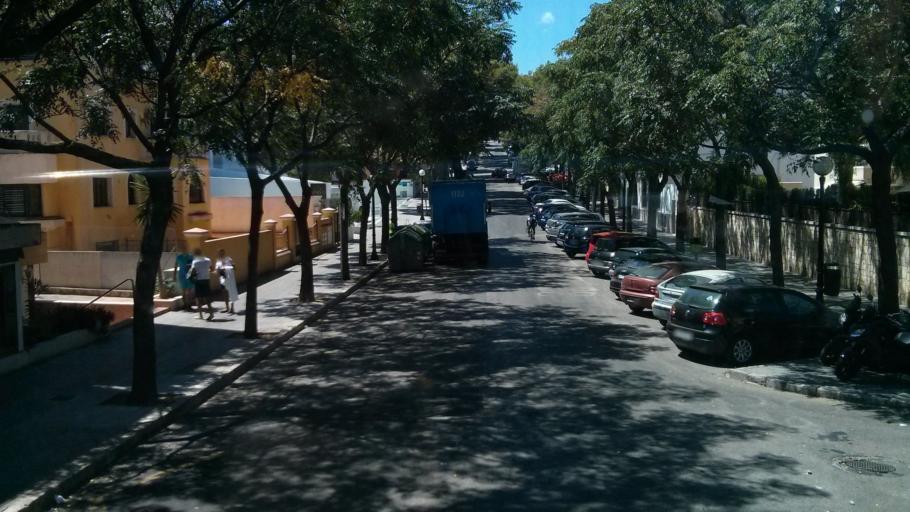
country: ES
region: Balearic Islands
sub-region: Illes Balears
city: Palma
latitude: 39.5669
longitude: 2.6268
